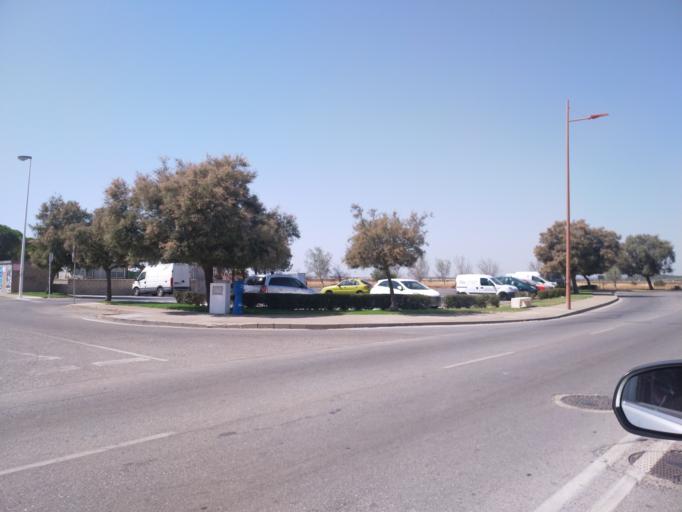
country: ES
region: Andalusia
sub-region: Provincia de Cadiz
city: Chiclana de la Frontera
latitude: 36.4287
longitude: -6.1511
